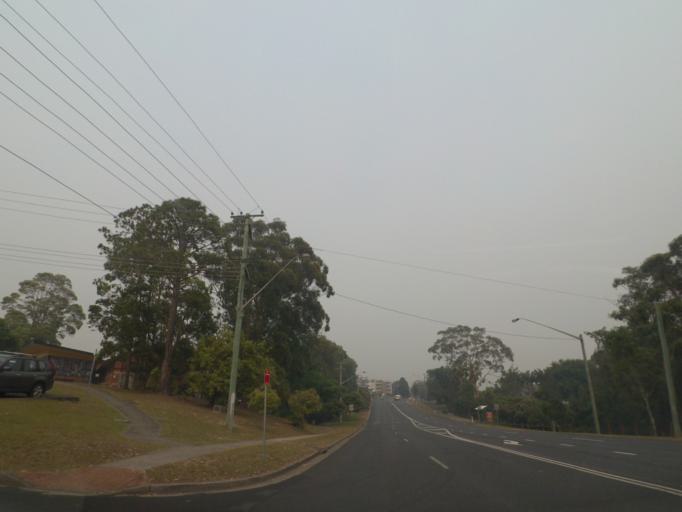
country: AU
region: New South Wales
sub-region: Coffs Harbour
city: Coffs Harbour
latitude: -30.3054
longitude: 153.1294
